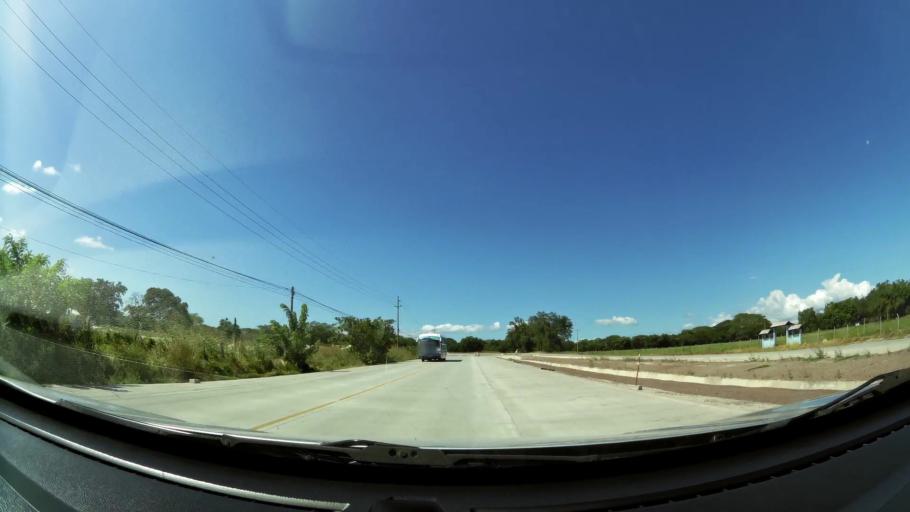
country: CR
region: Guanacaste
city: Bagaces
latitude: 10.5486
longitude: -85.3569
